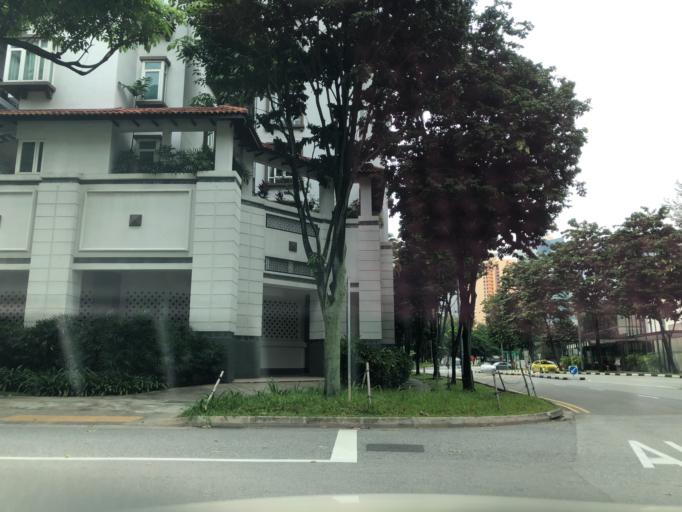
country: SG
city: Singapore
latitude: 1.2914
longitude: 103.8385
